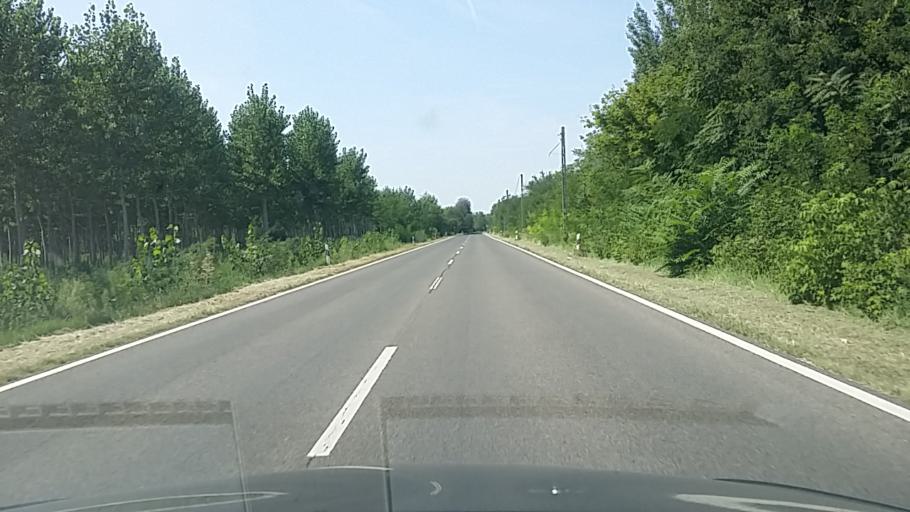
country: HU
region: Pest
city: Tapioszele
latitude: 47.3011
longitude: 19.8892
